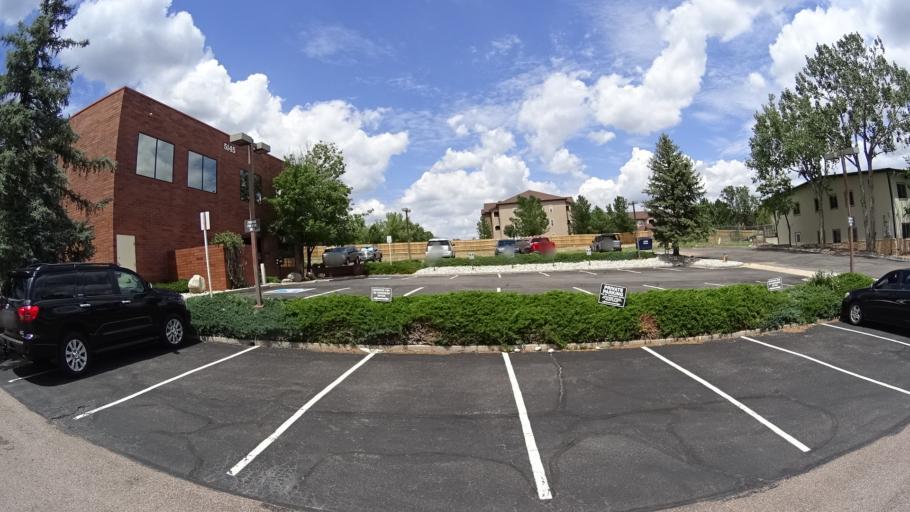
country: US
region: Colorado
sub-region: El Paso County
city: Manitou Springs
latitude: 38.9047
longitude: -104.8625
